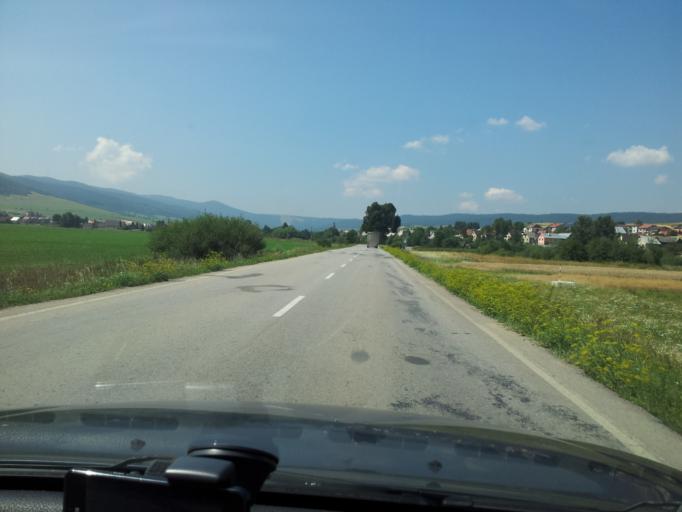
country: SK
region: Zilinsky
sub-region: Okres Dolny Kubin
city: Dolny Kubin
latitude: 49.3280
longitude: 19.3630
